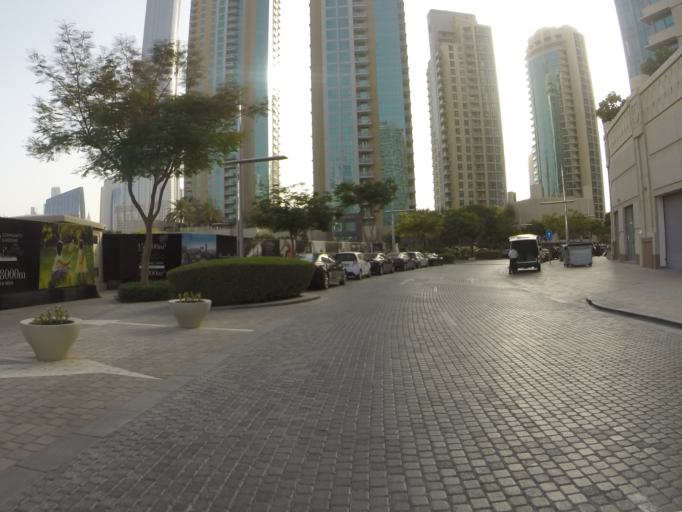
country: AE
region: Dubai
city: Dubai
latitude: 25.1925
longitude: 55.2715
